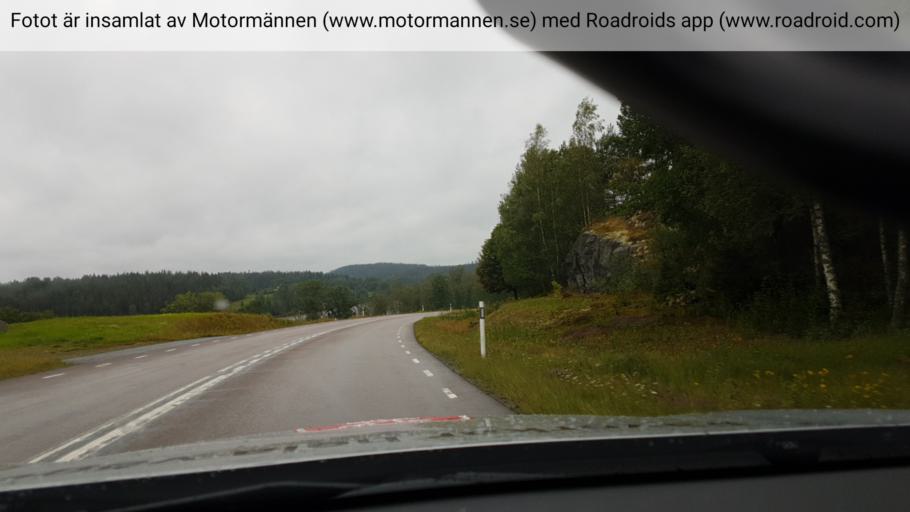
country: SE
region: Vaestra Goetaland
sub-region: Dals-Ed Kommun
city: Ed
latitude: 58.9262
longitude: 12.0357
